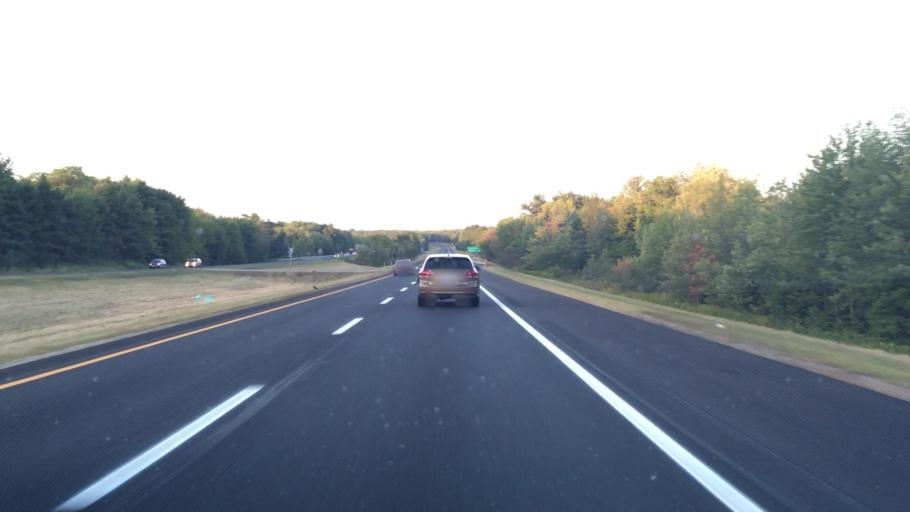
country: US
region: Maine
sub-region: Sagadahoc County
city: Topsham
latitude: 43.9505
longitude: -69.9698
